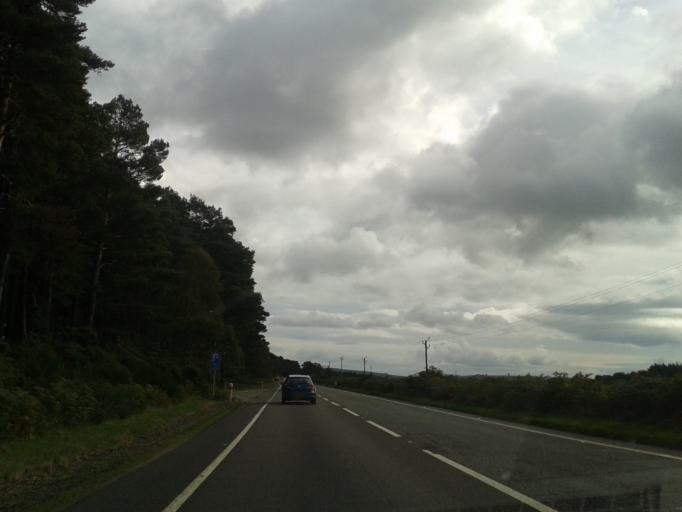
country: GB
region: Scotland
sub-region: Moray
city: Lhanbryd
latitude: 57.6323
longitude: -3.1826
